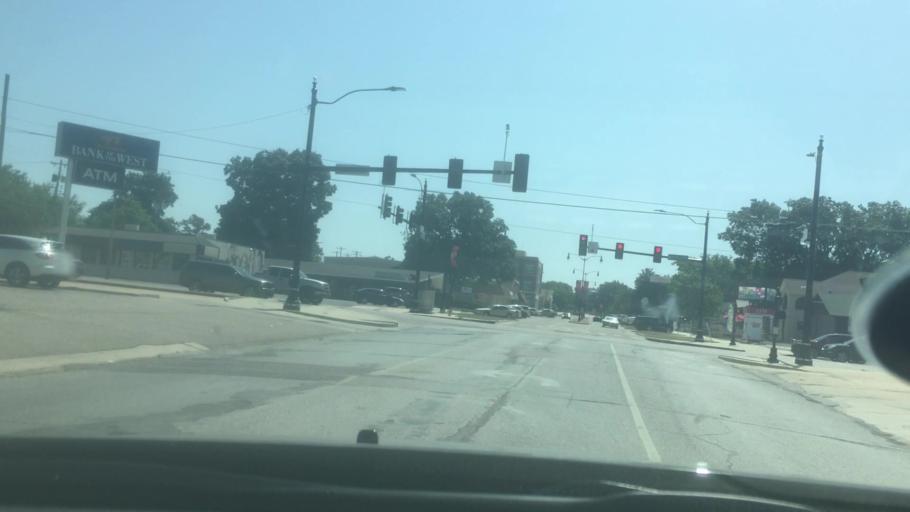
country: US
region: Oklahoma
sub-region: Pontotoc County
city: Ada
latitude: 34.7745
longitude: -96.6705
